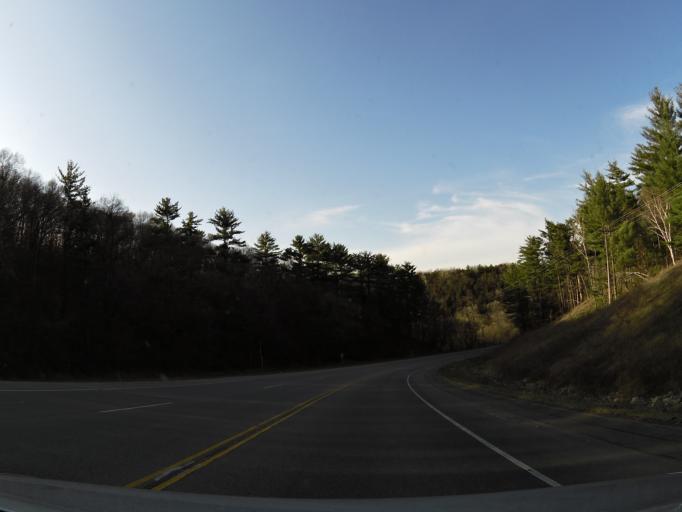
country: US
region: Minnesota
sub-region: Washington County
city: Afton
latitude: 44.8282
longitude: -92.7346
